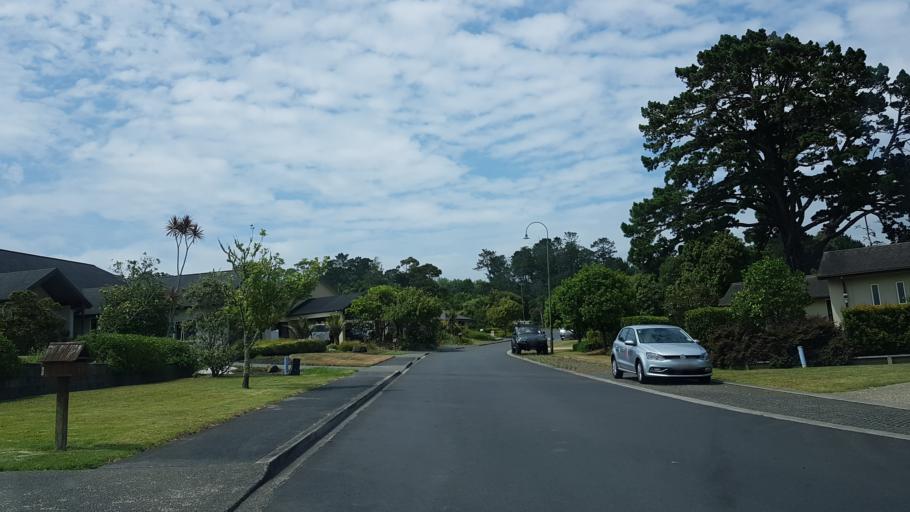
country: NZ
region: Auckland
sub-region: Auckland
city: North Shore
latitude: -36.7751
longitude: 174.6864
